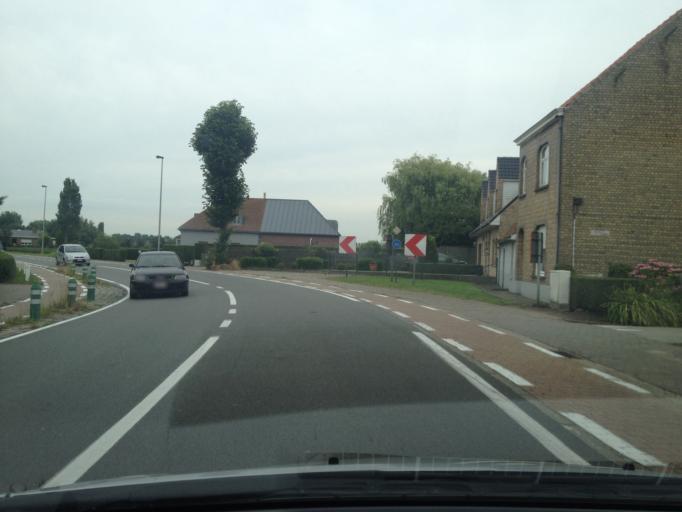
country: BE
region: Flanders
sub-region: Provincie West-Vlaanderen
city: Gistel
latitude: 51.1461
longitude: 2.9506
